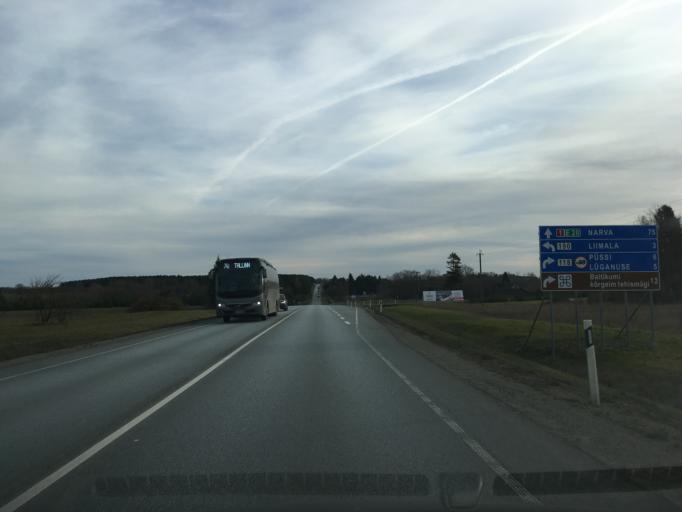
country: EE
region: Ida-Virumaa
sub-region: Kivioli linn
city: Kivioli
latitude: 59.4117
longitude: 26.9998
